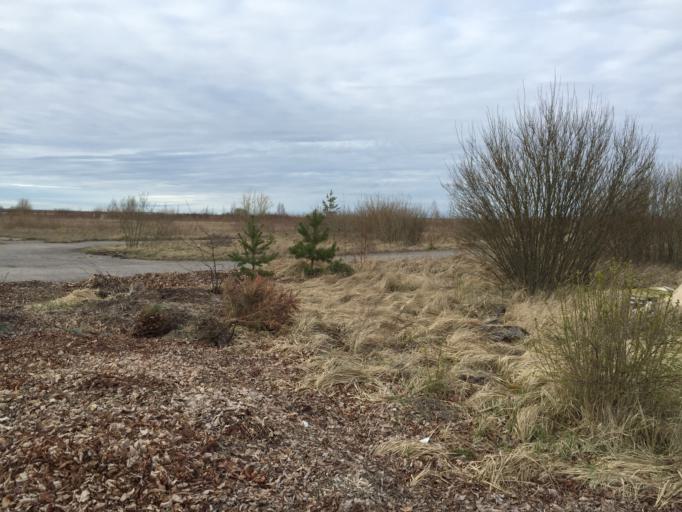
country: LT
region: Klaipedos apskritis
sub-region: Klaipeda
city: Klaipeda
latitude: 55.7097
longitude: 21.2470
